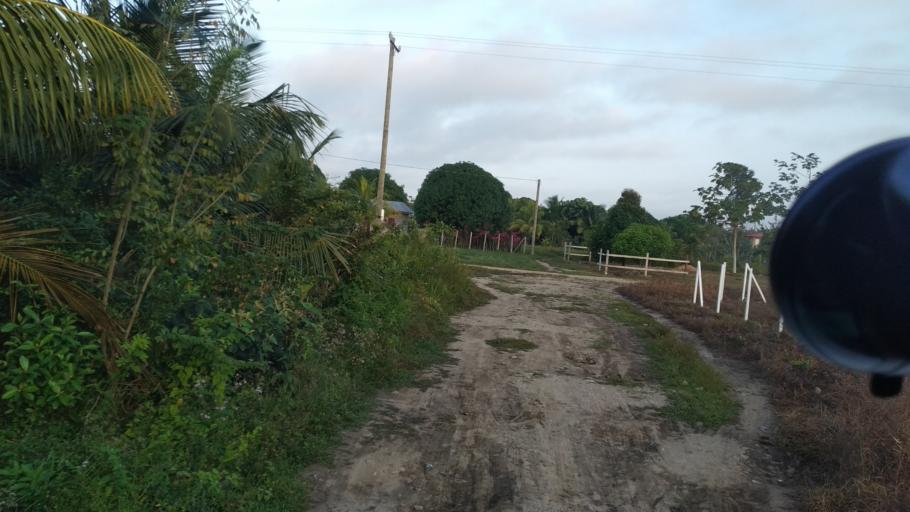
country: BZ
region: Stann Creek
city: Placencia
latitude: 16.5692
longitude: -88.5248
